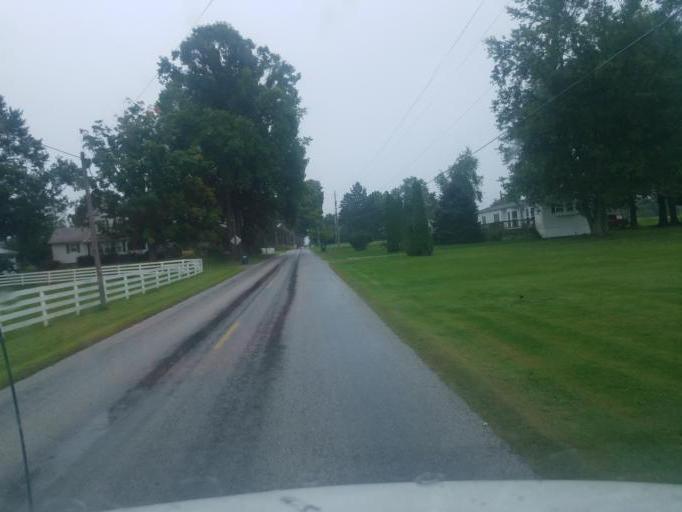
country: US
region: Ohio
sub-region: Wayne County
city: Creston
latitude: 40.9843
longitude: -81.8831
